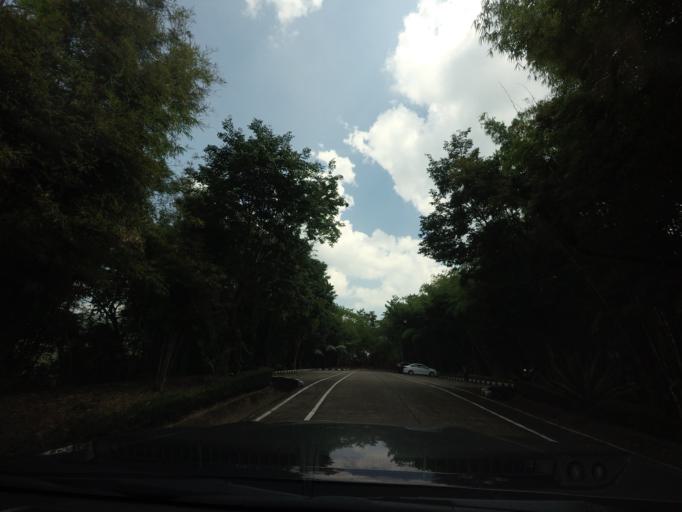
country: TH
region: Nan
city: Bo Kluea
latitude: 19.0196
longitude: 101.2095
